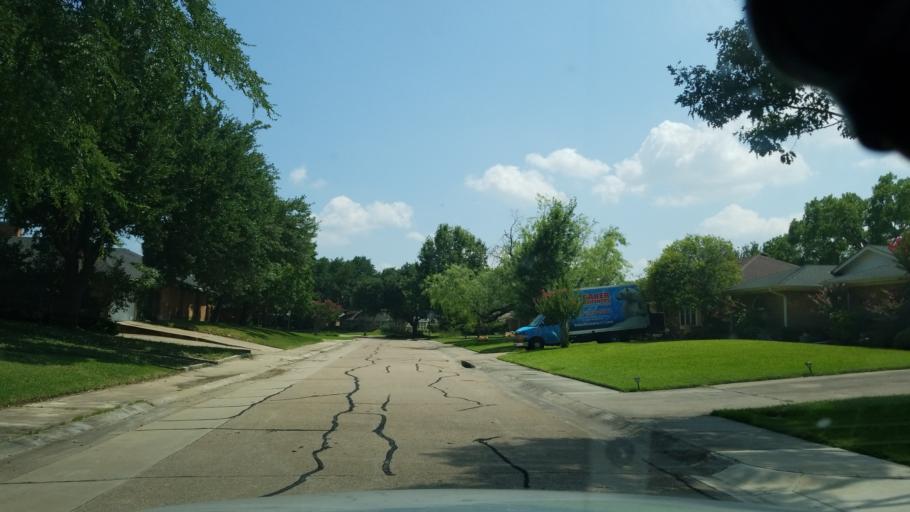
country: US
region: Texas
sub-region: Dallas County
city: Carrollton
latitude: 32.9640
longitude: -96.8637
